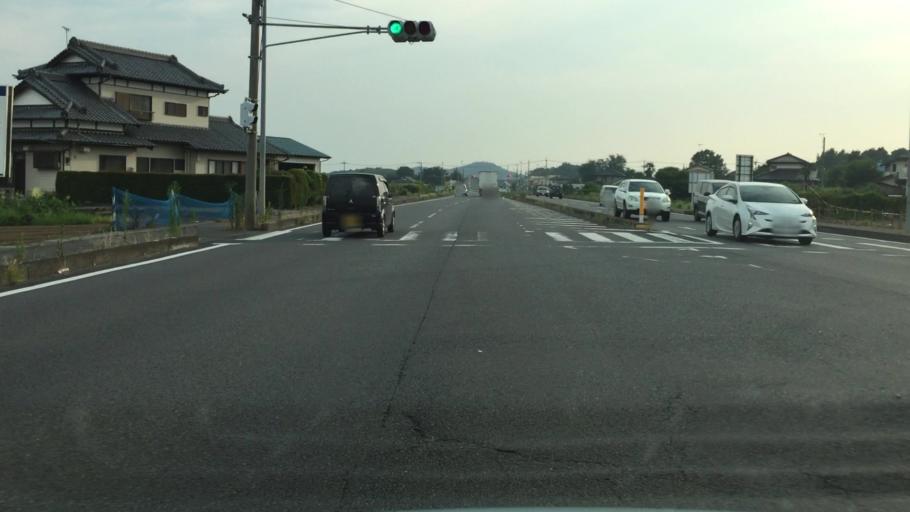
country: JP
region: Tochigi
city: Tochigi
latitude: 36.3303
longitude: 139.6901
